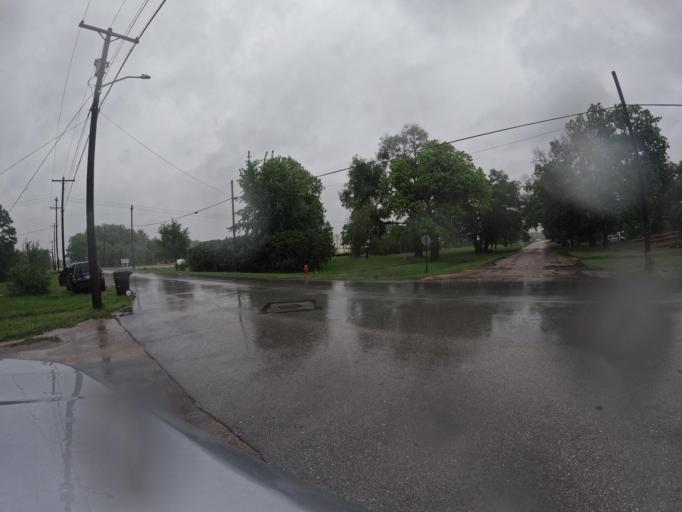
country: US
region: Nebraska
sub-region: Gage County
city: Wymore
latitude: 40.1225
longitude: -96.6593
